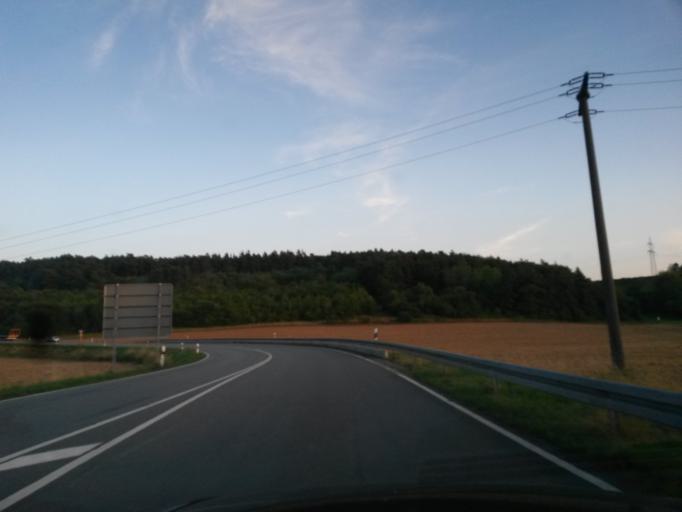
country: DE
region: Bavaria
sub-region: Regierungsbezirk Unterfranken
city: Marktheidenfeld
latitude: 49.8151
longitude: 9.6366
